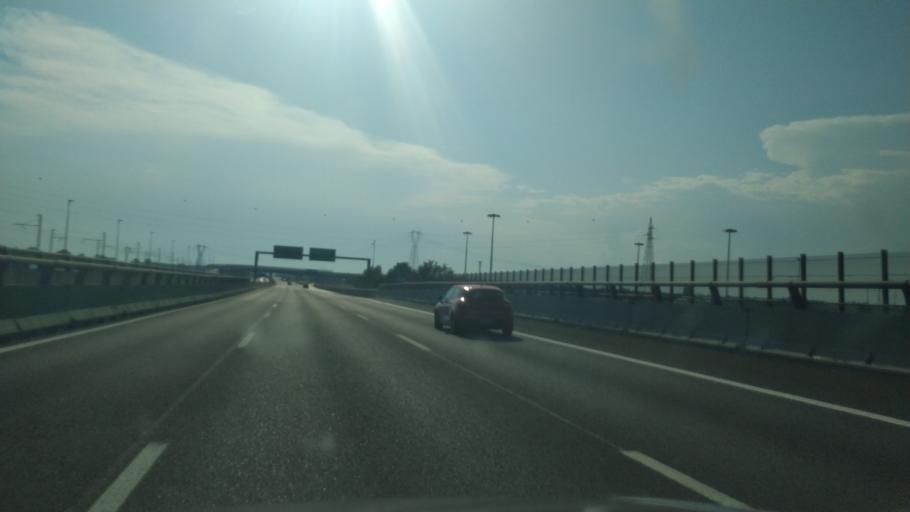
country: IT
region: Piedmont
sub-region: Provincia di Novara
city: San Pietro Mosezzo
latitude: 45.4743
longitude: 8.5747
